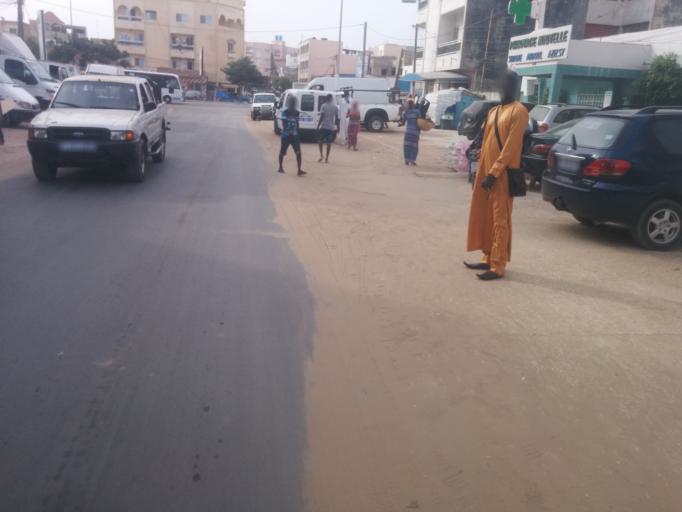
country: SN
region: Dakar
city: Grand Dakar
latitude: 14.7512
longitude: -17.4405
